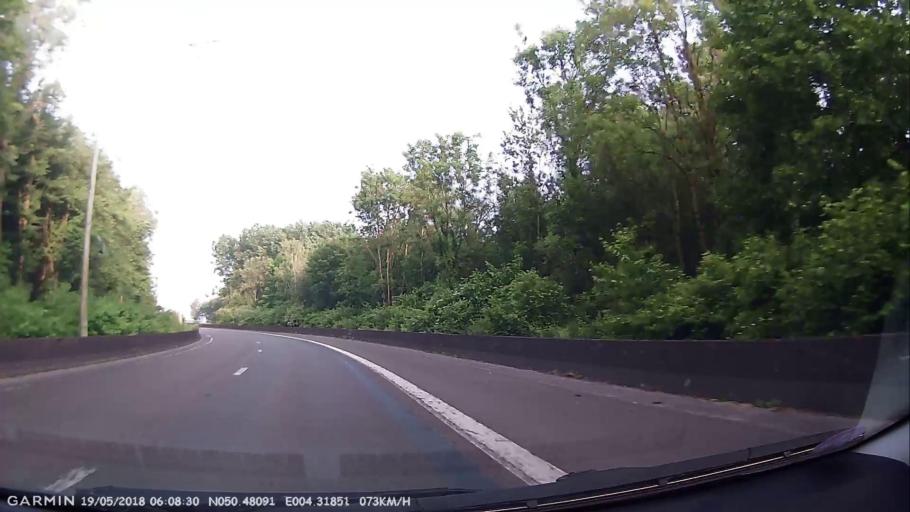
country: BE
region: Wallonia
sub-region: Province du Hainaut
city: Chapelle-lez-Herlaimont
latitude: 50.4809
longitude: 4.3186
